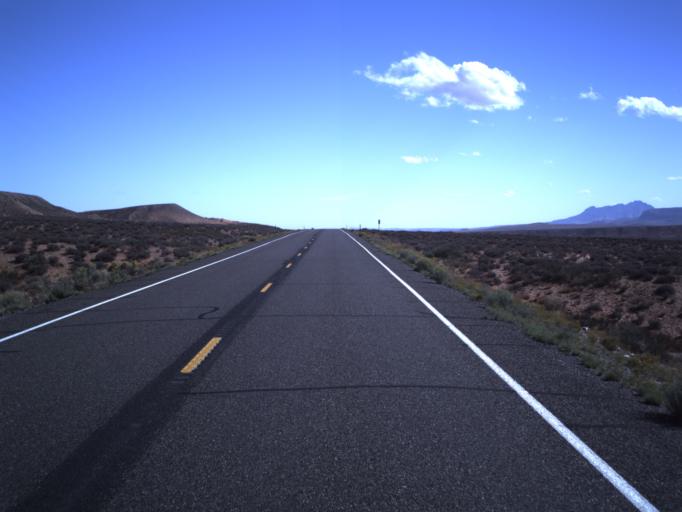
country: US
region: Utah
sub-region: Wayne County
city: Loa
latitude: 38.0897
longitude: -110.6175
